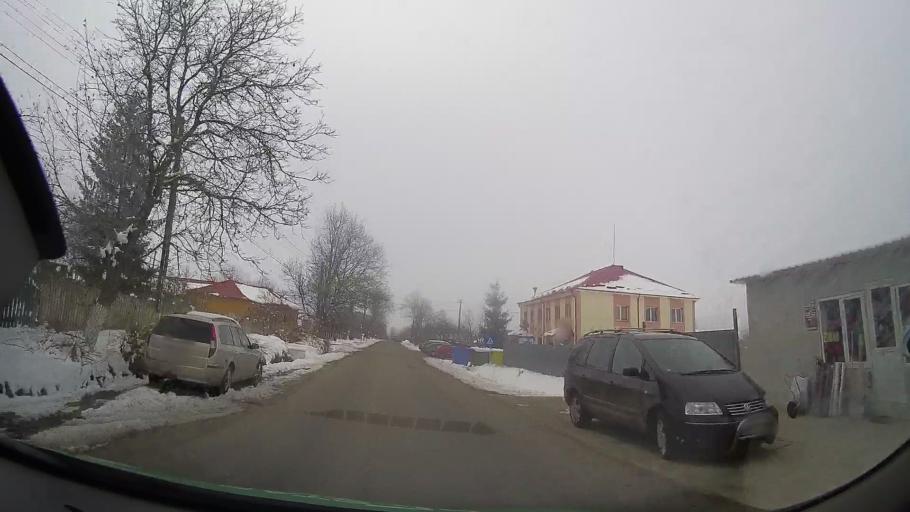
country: RO
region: Bacau
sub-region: Comuna Stanisesti
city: Stanisesti
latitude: 46.4055
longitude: 27.2726
